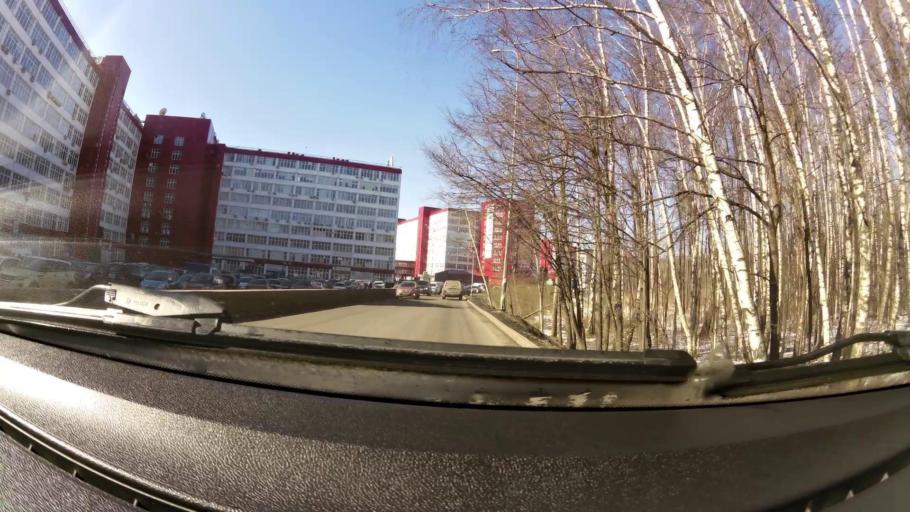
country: RU
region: Moskovskaya
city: Mosrentgen
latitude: 55.6347
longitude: 37.4433
